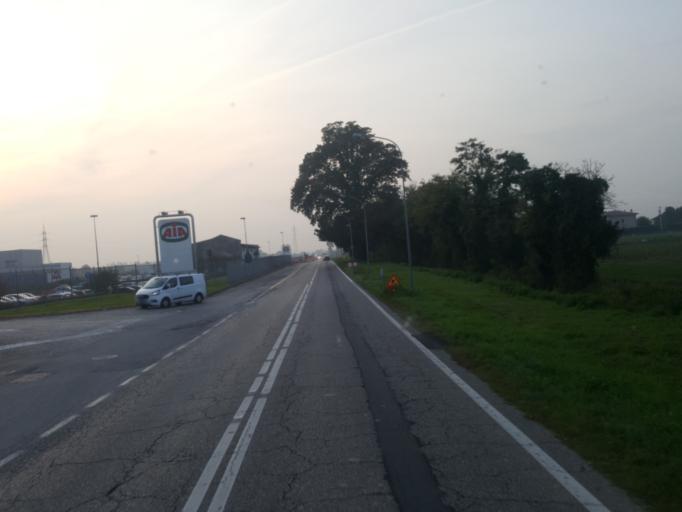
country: IT
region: Veneto
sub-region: Provincia di Verona
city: Zevio
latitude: 45.3721
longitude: 11.0912
